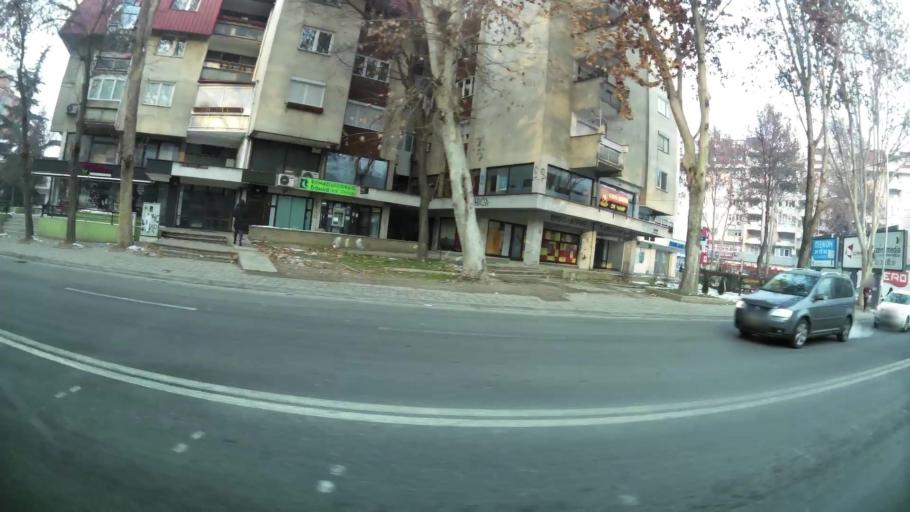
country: MK
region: Cair
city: Cair
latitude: 42.0136
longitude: 21.4456
